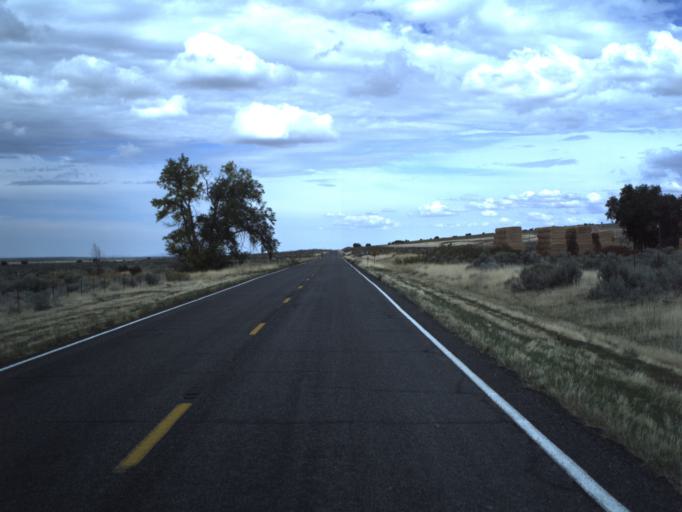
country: US
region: Utah
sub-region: Millard County
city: Fillmore
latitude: 38.9869
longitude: -112.4106
